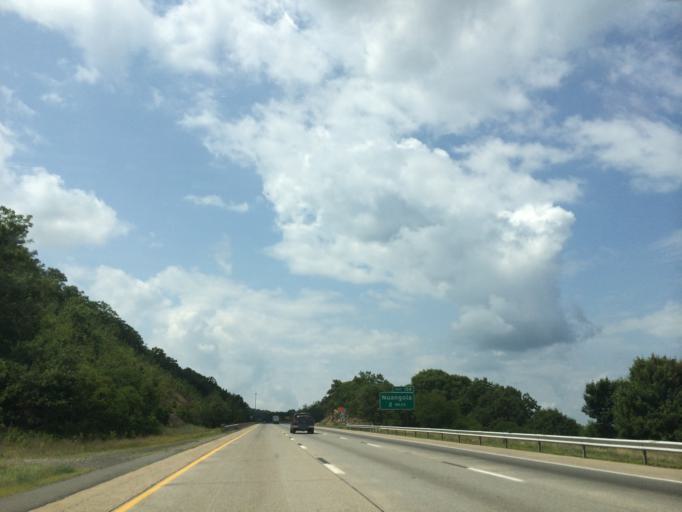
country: US
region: Pennsylvania
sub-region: Luzerne County
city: Ashley
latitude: 41.1770
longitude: -75.9456
